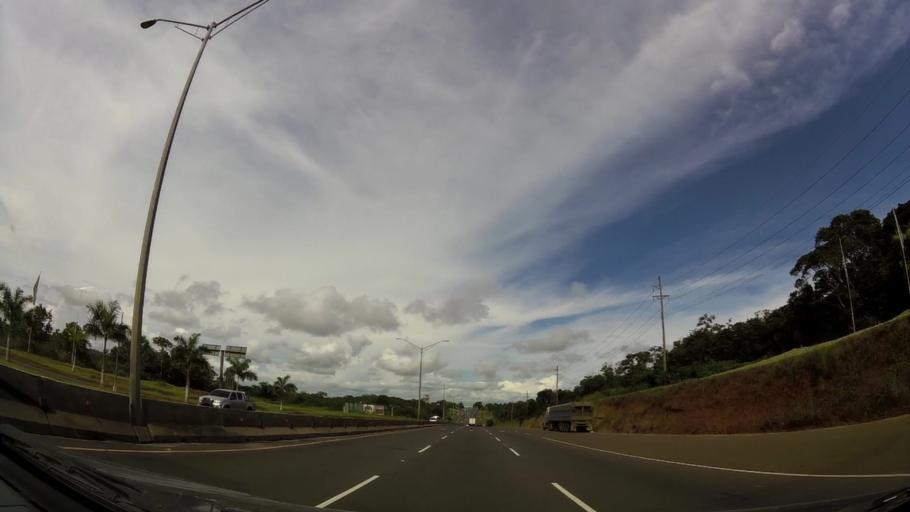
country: PA
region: Panama
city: La Chorrera
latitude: 8.8833
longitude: -79.7572
